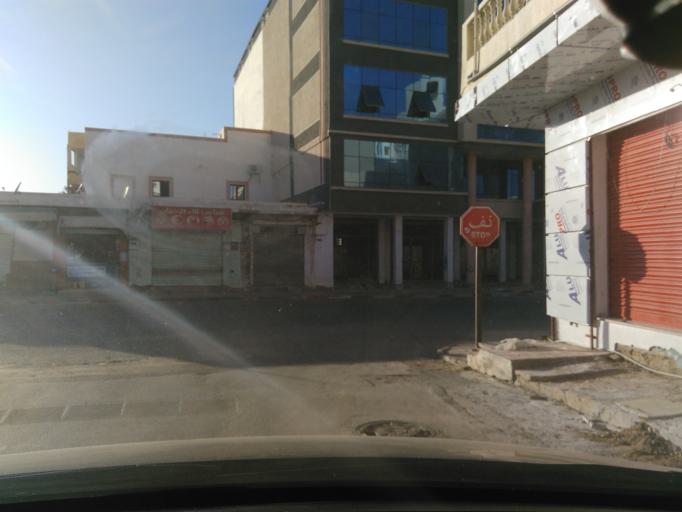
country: TN
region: Tataouine
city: Tataouine
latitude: 32.9284
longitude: 10.4460
